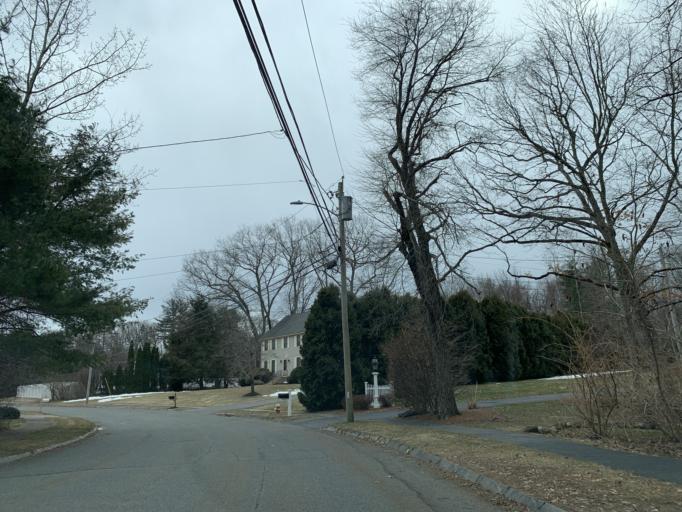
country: US
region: Massachusetts
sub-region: Norfolk County
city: Bellingham
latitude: 42.0436
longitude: -71.4460
